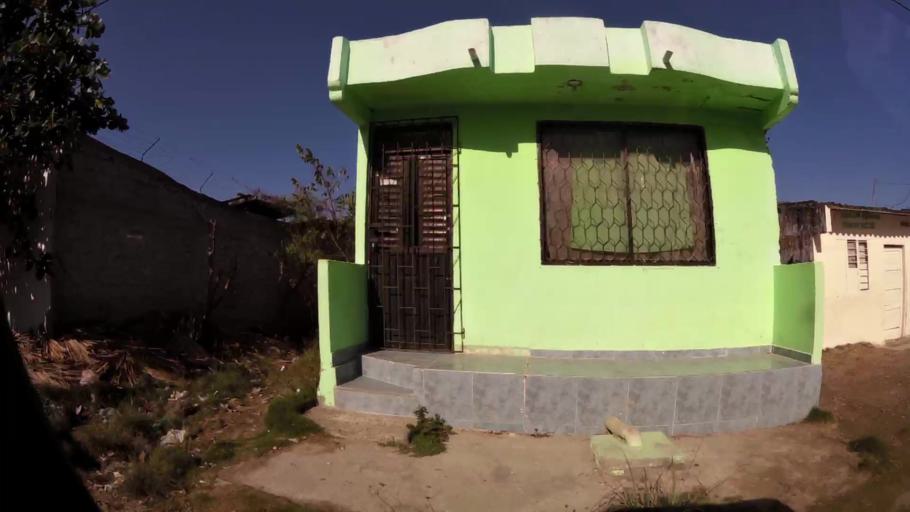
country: CO
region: Bolivar
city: Cartagena
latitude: 10.4848
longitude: -75.4914
